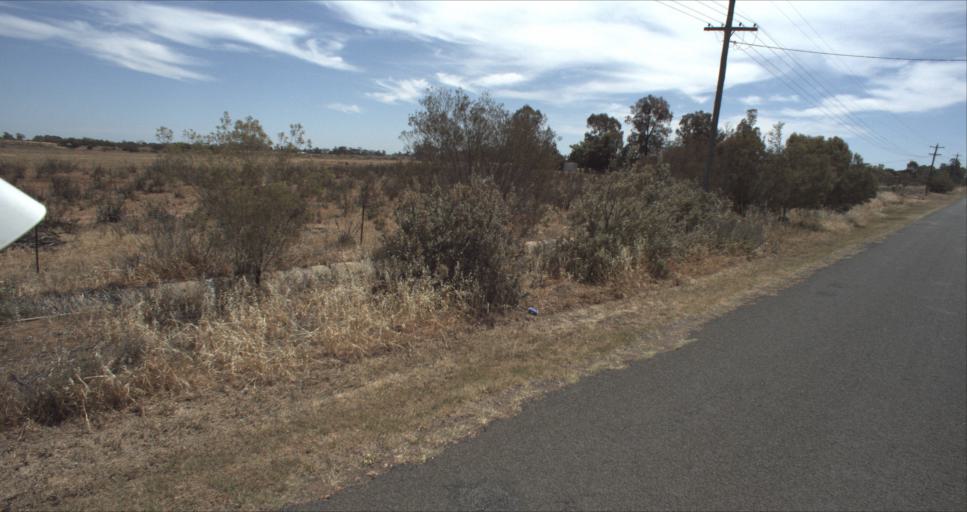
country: AU
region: New South Wales
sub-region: Leeton
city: Leeton
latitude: -34.5991
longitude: 146.4273
